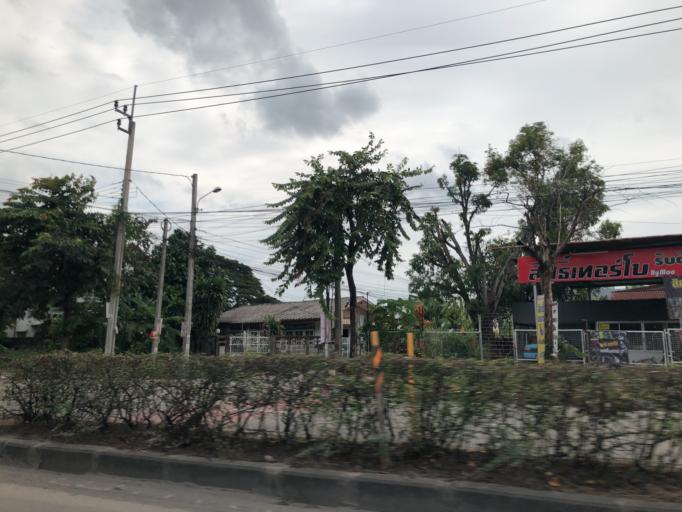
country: TH
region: Nonthaburi
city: Pak Kret
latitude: 13.9176
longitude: 100.5245
